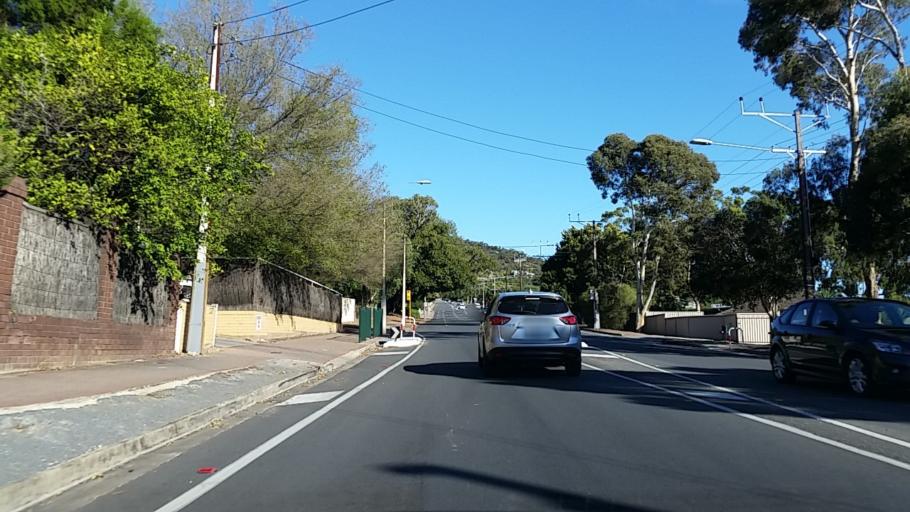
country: AU
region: South Australia
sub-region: Mitcham
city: Clapham
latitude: -34.9878
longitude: 138.6103
